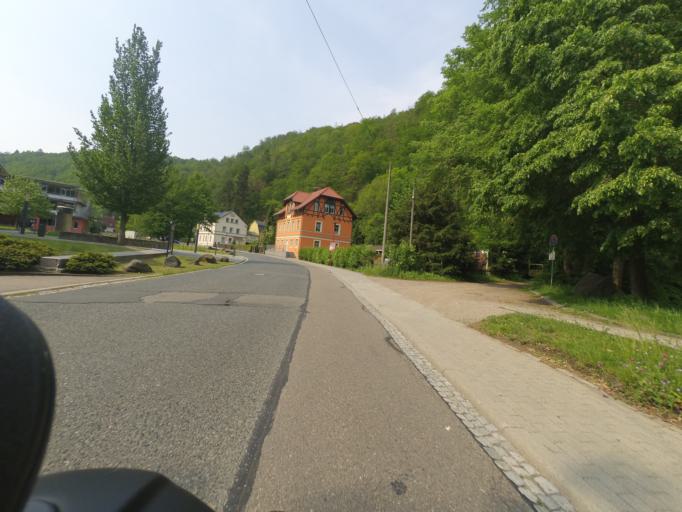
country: DE
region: Saxony
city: Tharandt
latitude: 50.9809
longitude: 13.5811
